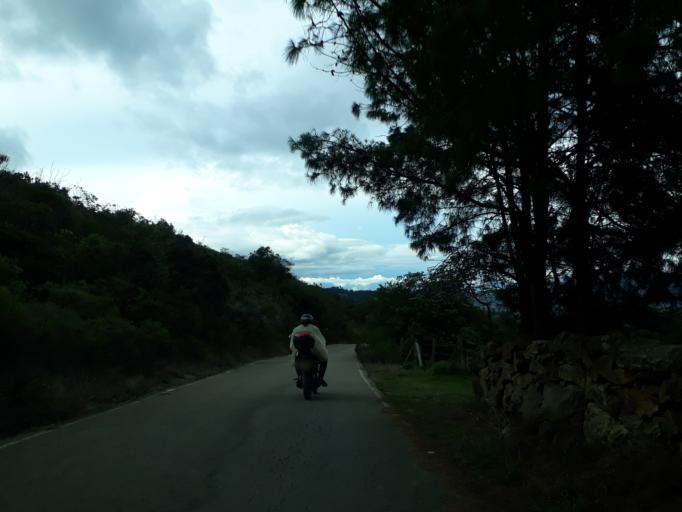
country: CO
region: Cundinamarca
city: Susa
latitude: 5.3962
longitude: -73.7818
